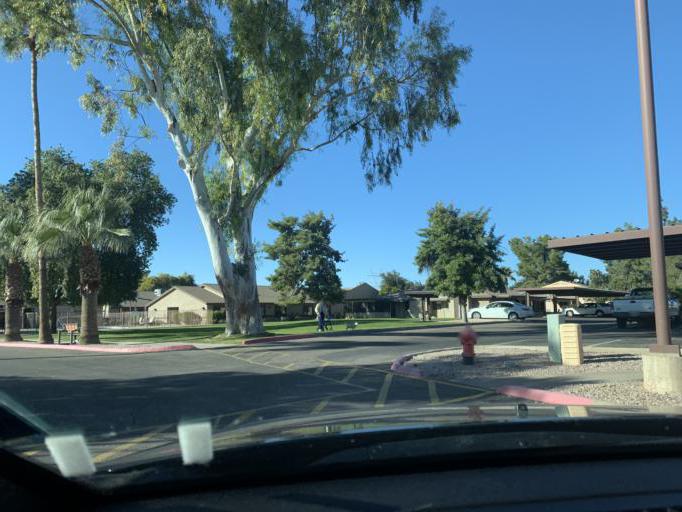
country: US
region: Arizona
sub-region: Maricopa County
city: Gilbert
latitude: 33.4239
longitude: -111.7039
